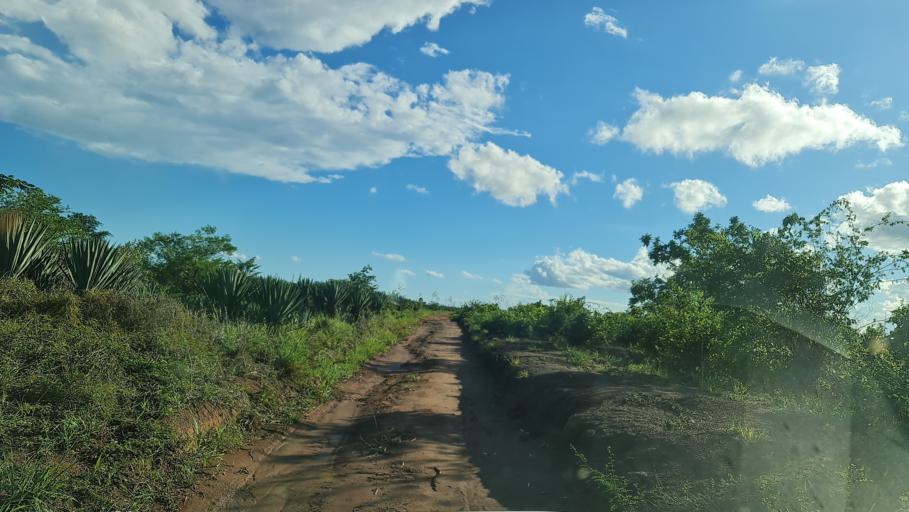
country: MZ
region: Nampula
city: Ilha de Mocambique
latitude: -14.9410
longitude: 40.1996
